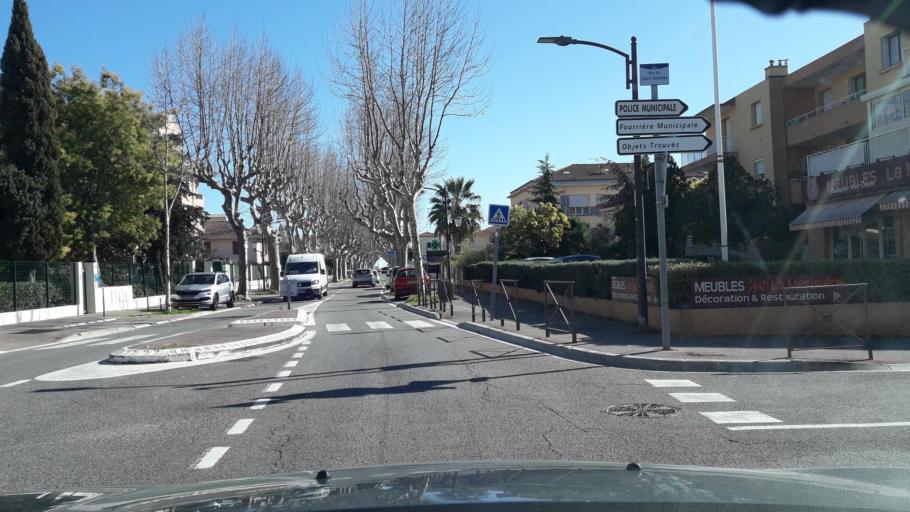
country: FR
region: Provence-Alpes-Cote d'Azur
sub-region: Departement du Var
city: Frejus
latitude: 43.4224
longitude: 6.7423
